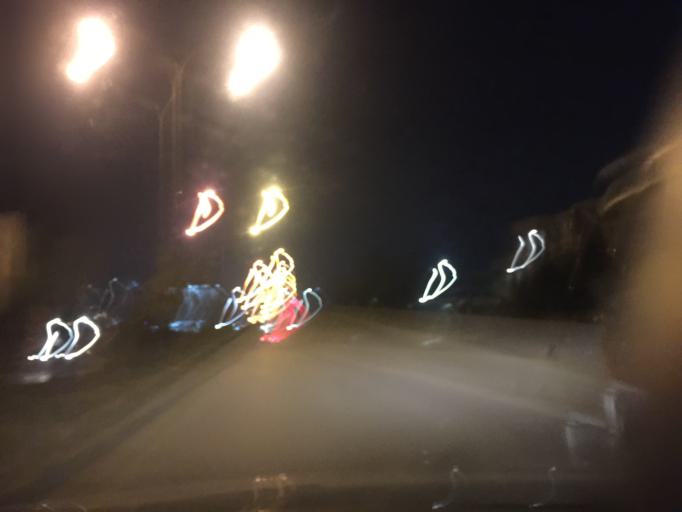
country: JO
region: Amman
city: Umm as Summaq
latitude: 31.8974
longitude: 35.8516
